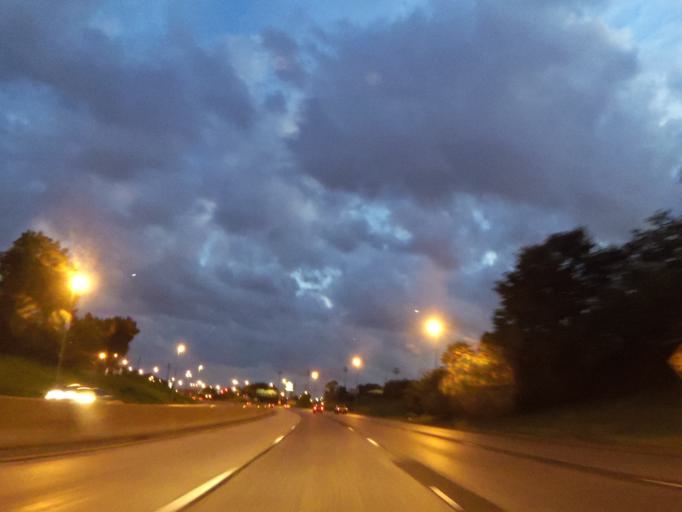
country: US
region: Missouri
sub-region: Saint Louis County
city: Lemay
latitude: 38.5602
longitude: -90.2557
